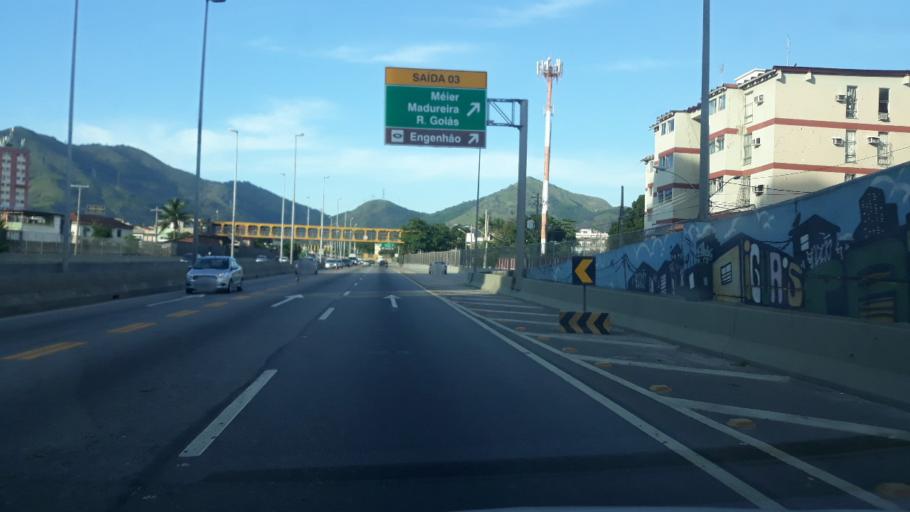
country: BR
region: Rio de Janeiro
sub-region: Rio De Janeiro
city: Rio de Janeiro
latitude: -22.8898
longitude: -43.2962
